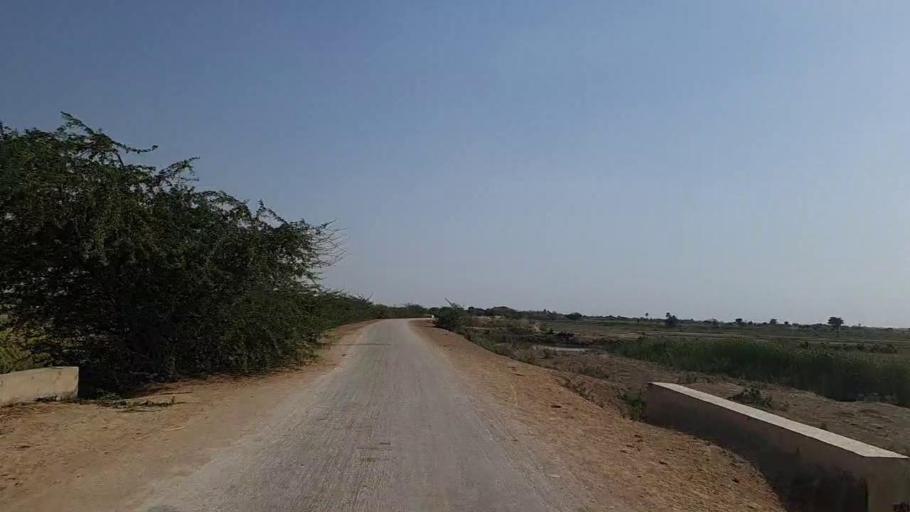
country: PK
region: Sindh
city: Daro Mehar
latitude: 24.7737
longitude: 68.1811
